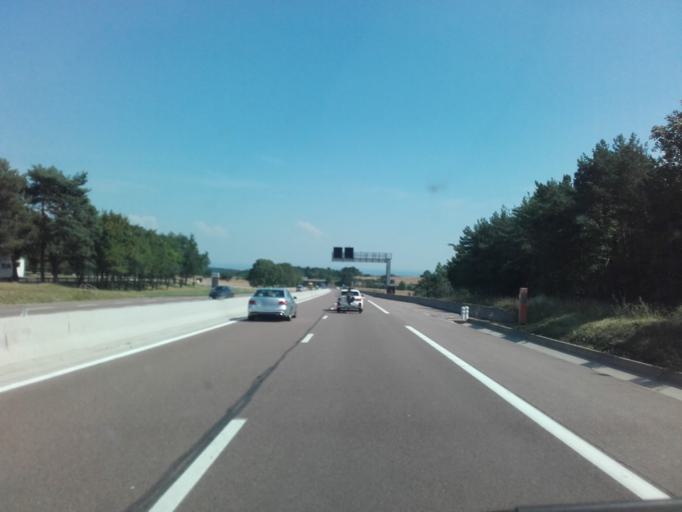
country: FR
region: Bourgogne
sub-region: Departement de la Cote-d'Or
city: Savigny-les-Beaune
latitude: 47.0625
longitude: 4.7722
